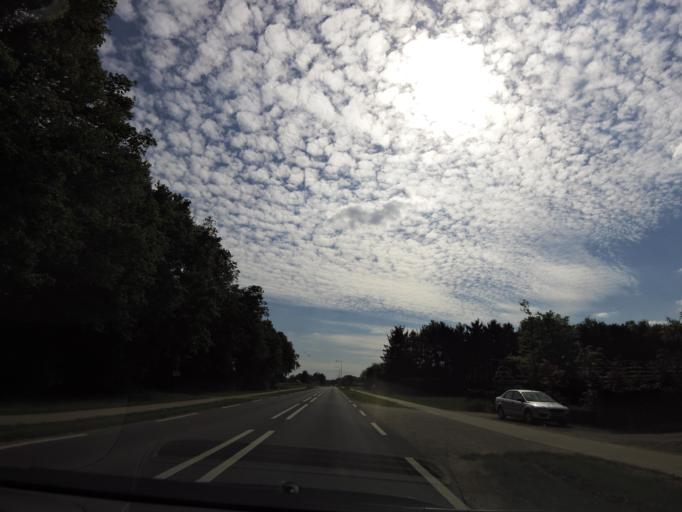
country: DE
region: North Rhine-Westphalia
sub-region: Regierungsbezirk Koln
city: Waldfeucht
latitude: 51.0777
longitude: 5.9795
